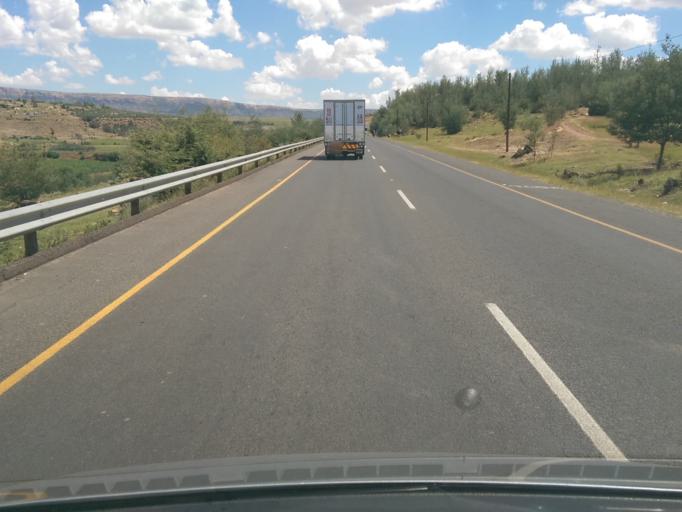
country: LS
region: Maseru
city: Maseru
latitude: -29.3981
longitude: 27.5348
